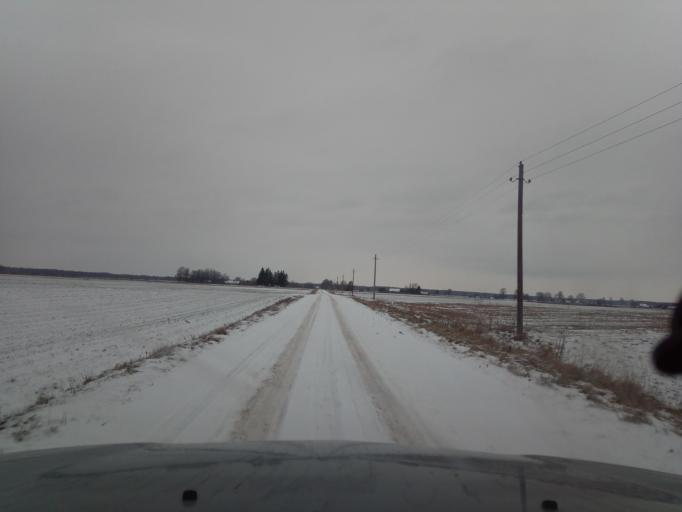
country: LT
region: Vilnius County
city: Ukmerge
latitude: 55.4812
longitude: 24.6101
